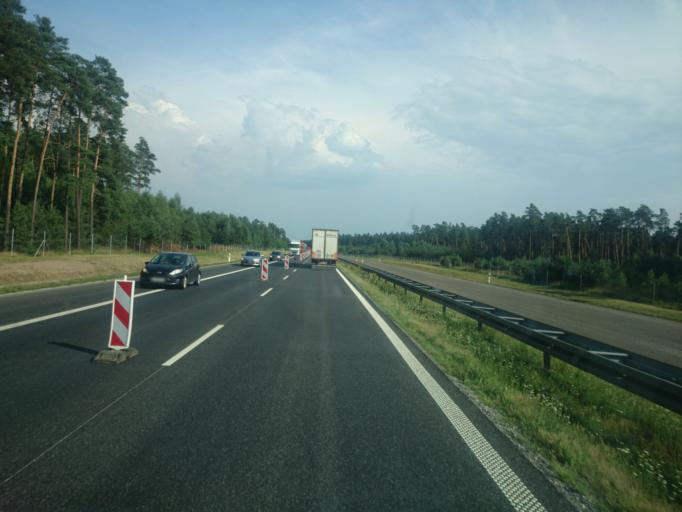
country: PL
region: Opole Voivodeship
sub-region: Powiat opolski
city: Komprachcice
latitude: 50.5920
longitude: 17.8073
